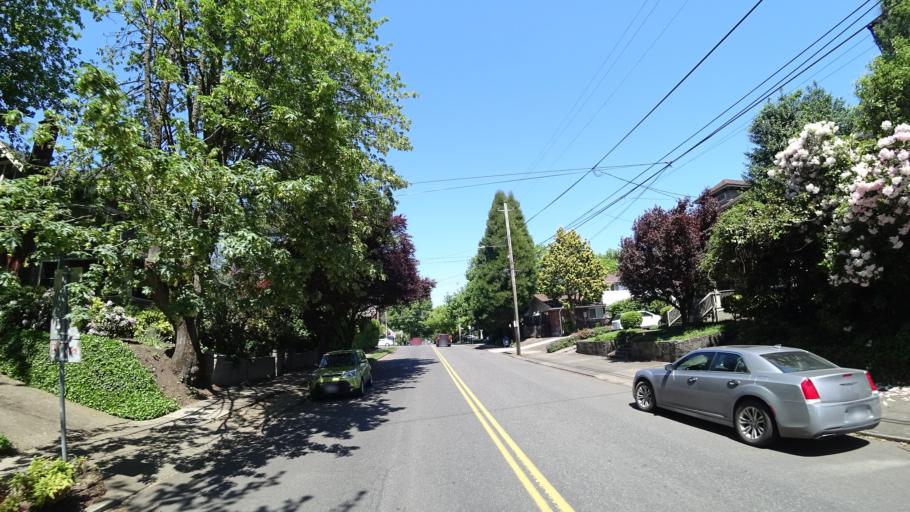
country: US
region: Oregon
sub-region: Multnomah County
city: Portland
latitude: 45.5416
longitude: -122.6505
